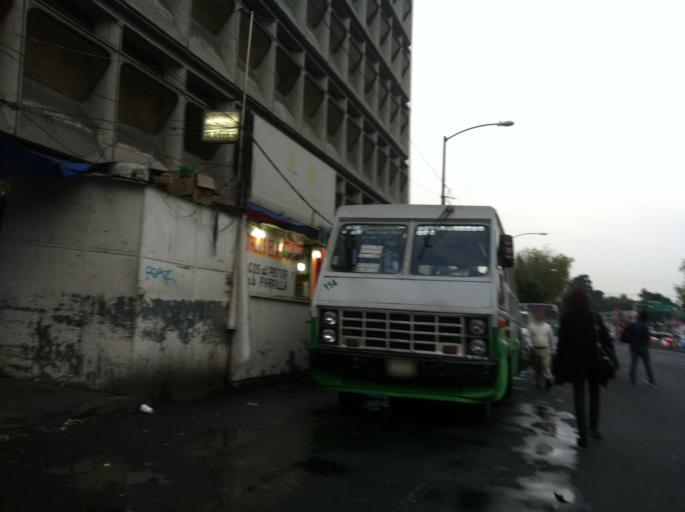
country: MX
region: Mexico City
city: Miguel Hidalgo
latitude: 19.4575
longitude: -99.1816
